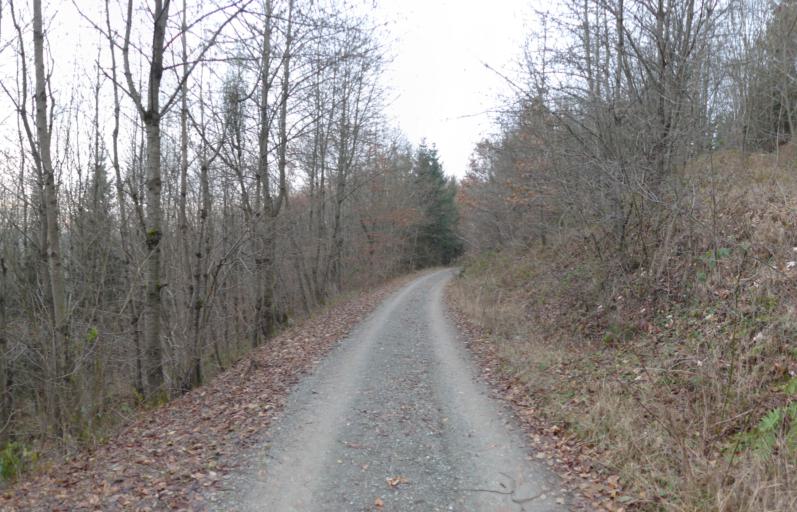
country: DE
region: Bavaria
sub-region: Upper Franconia
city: Stadtsteinach
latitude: 50.1771
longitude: 11.4980
